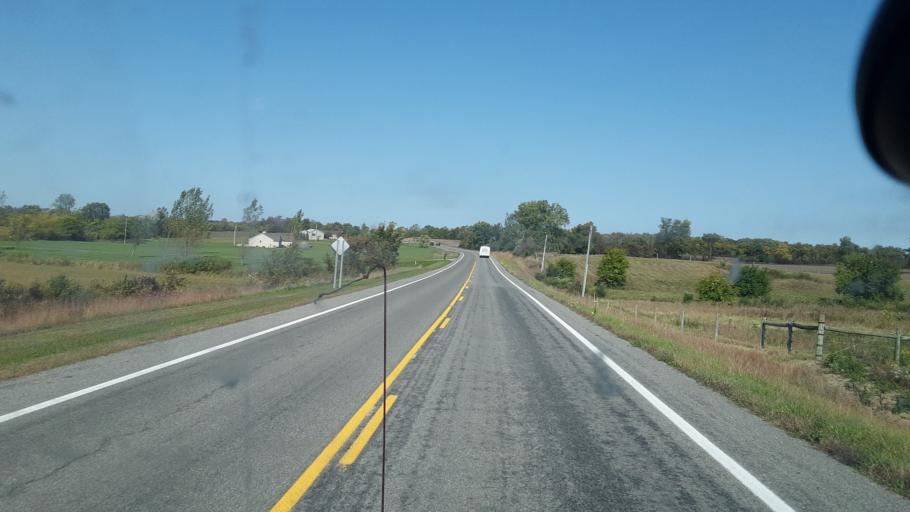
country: US
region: Ohio
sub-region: Logan County
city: Northwood
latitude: 40.4565
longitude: -83.7279
